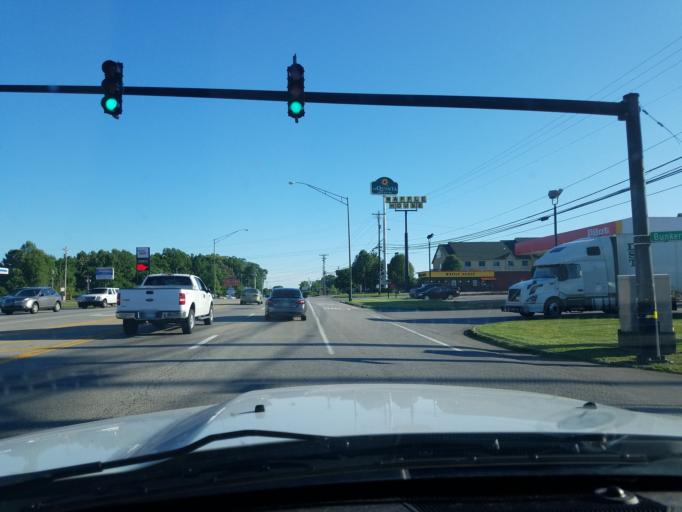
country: US
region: Tennessee
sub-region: Putnam County
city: Cookeville
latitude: 36.1340
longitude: -85.5035
